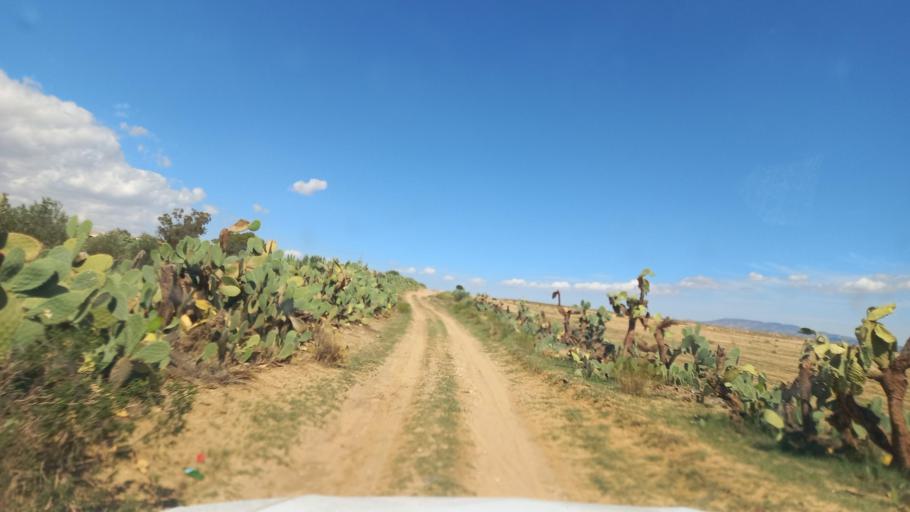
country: TN
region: Al Qasrayn
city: Sbiba
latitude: 35.3456
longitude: 9.0129
